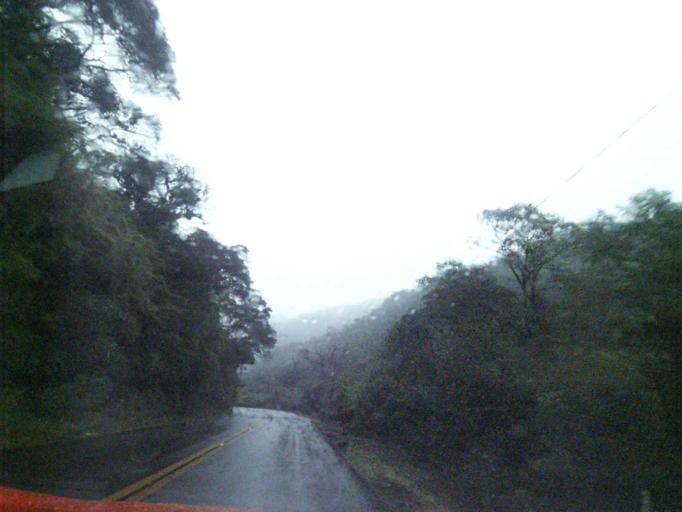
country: BR
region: Santa Catarina
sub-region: Anitapolis
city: Anitapolis
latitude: -27.7602
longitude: -49.0374
